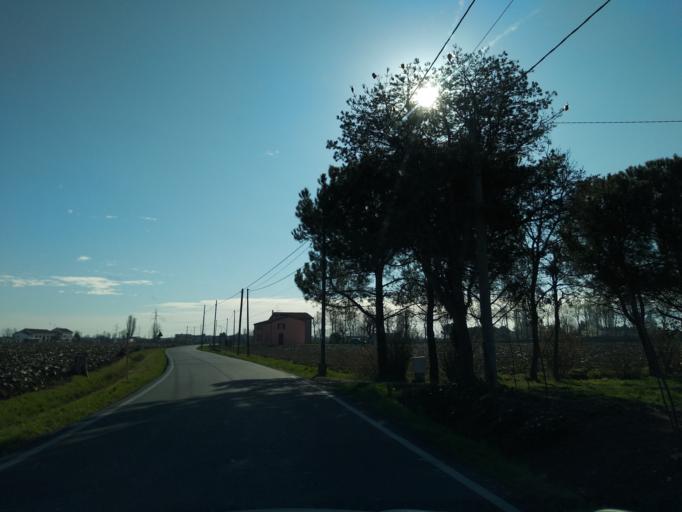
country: IT
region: Veneto
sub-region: Provincia di Padova
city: Bosco
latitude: 45.4526
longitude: 11.7975
